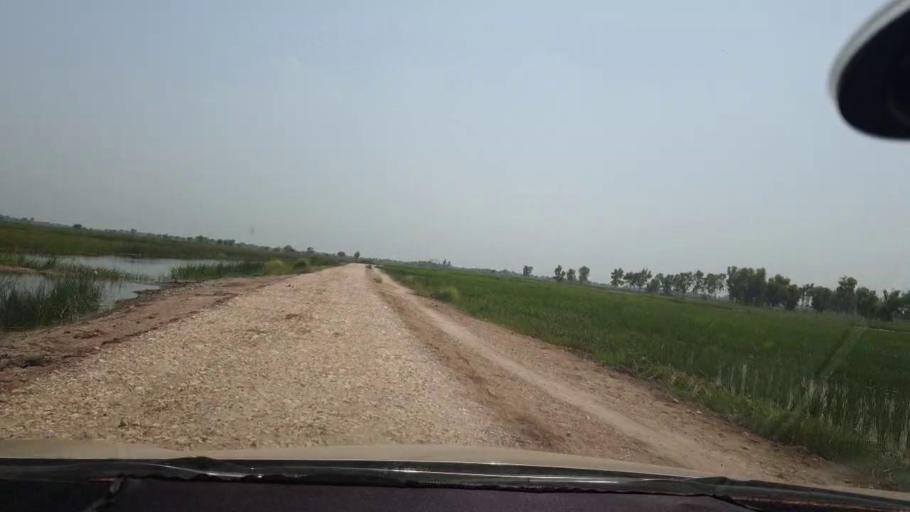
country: PK
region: Sindh
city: Kambar
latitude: 27.6525
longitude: 67.9317
